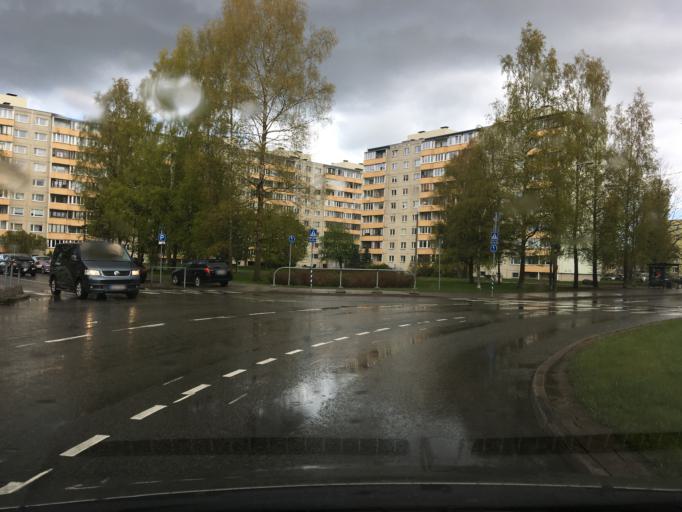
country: EE
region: Harju
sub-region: Tallinna linn
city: Kose
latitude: 59.4411
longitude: 24.8779
